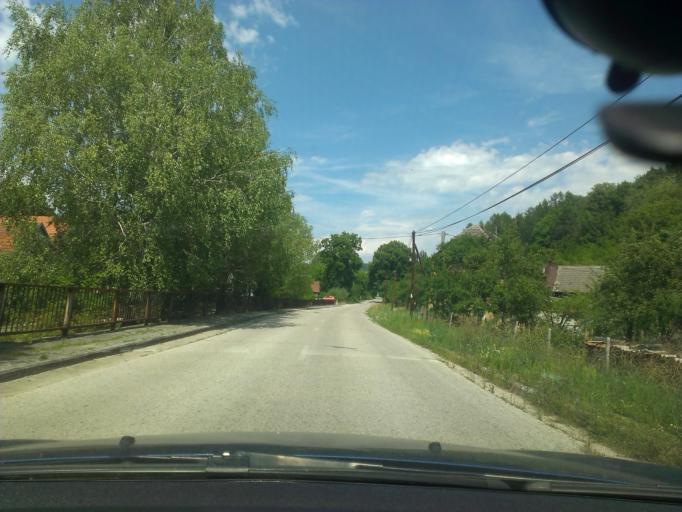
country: SK
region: Trenciansky
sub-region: Okres Myjava
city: Myjava
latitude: 48.7845
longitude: 17.5630
